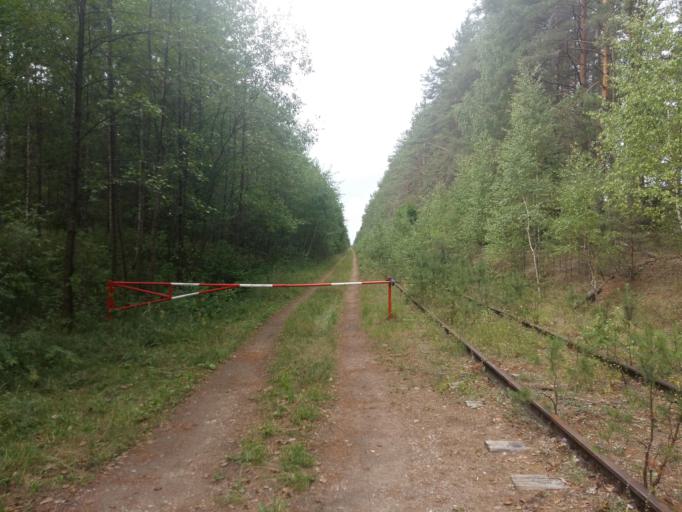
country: LT
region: Alytaus apskritis
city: Druskininkai
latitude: 53.9496
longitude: 24.2339
